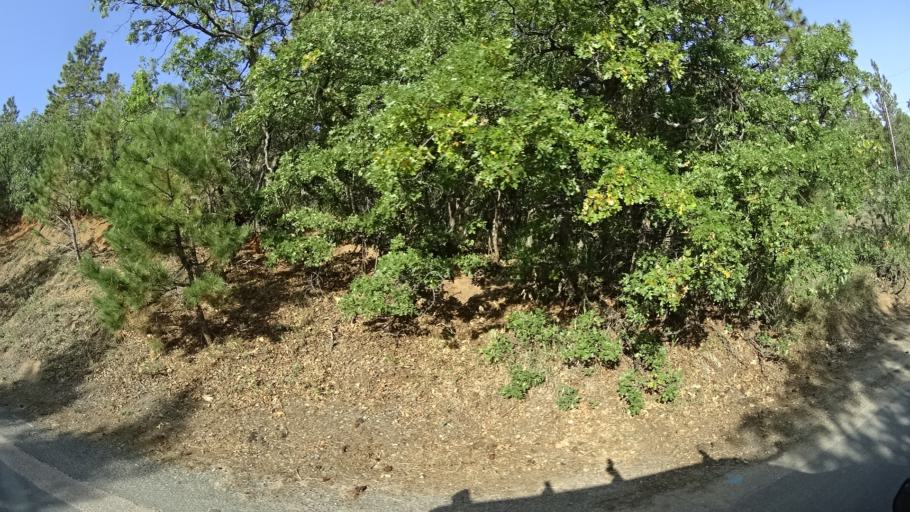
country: US
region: Colorado
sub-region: El Paso County
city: Colorado Springs
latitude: 38.8107
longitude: -104.8733
